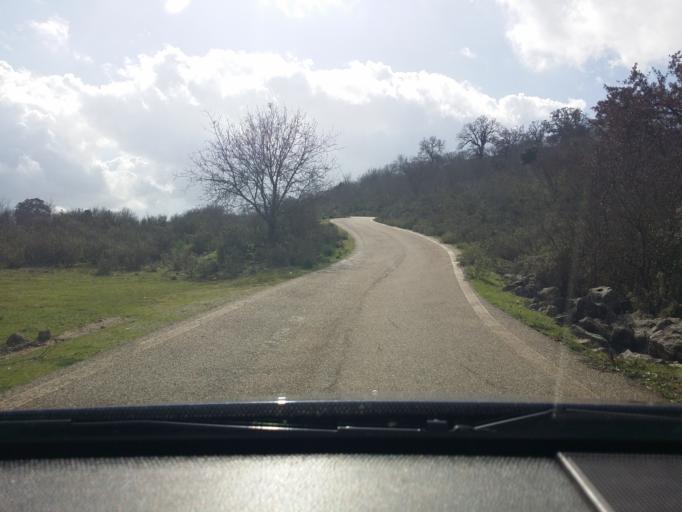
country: GR
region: West Greece
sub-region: Nomos Aitolias kai Akarnanias
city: Fitiai
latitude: 38.6407
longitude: 21.1959
